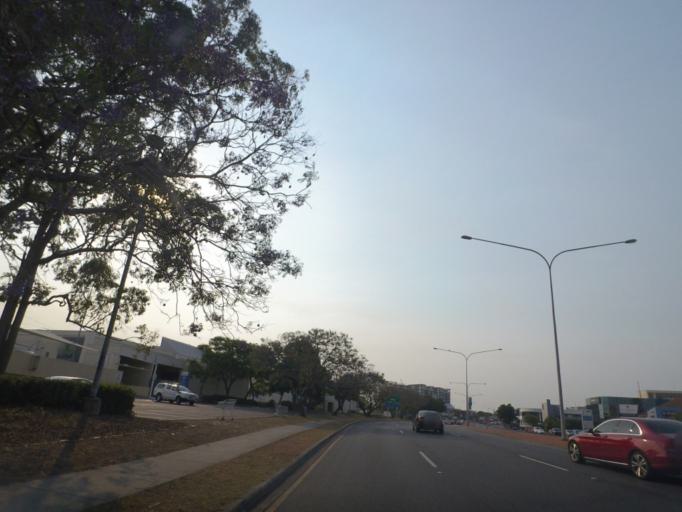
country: AU
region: Queensland
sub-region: Brisbane
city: Upper Mount Gravatt
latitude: -27.5616
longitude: 153.0833
